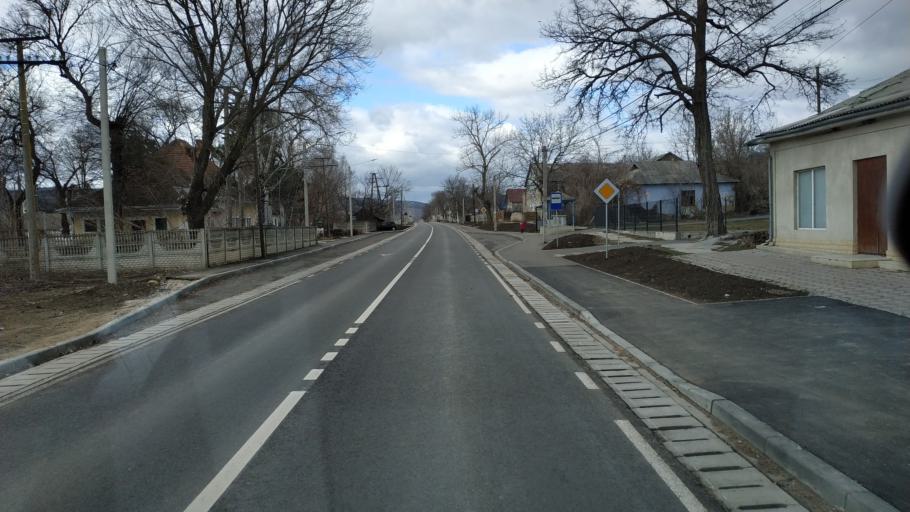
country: MD
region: Stinga Nistrului
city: Bucovat
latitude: 47.1877
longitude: 28.4580
